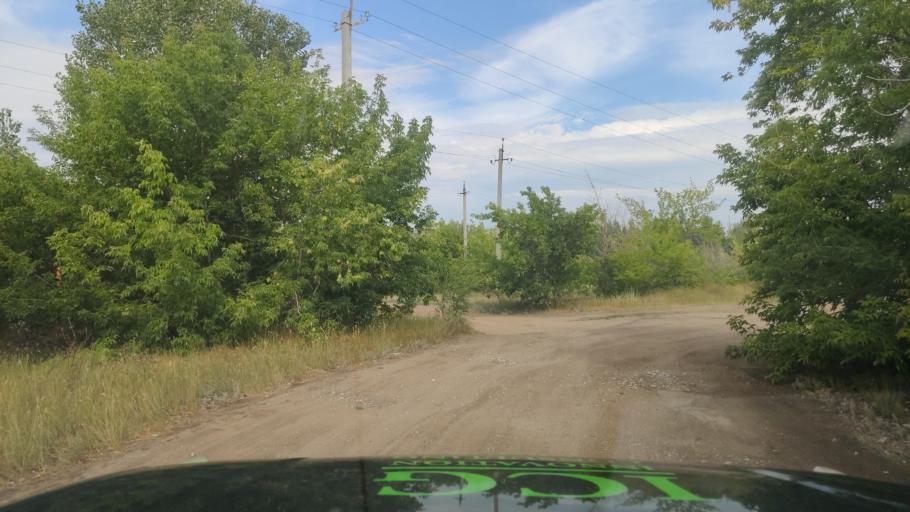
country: KZ
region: Pavlodar
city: Leninskiy
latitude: 52.4964
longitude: 76.8212
